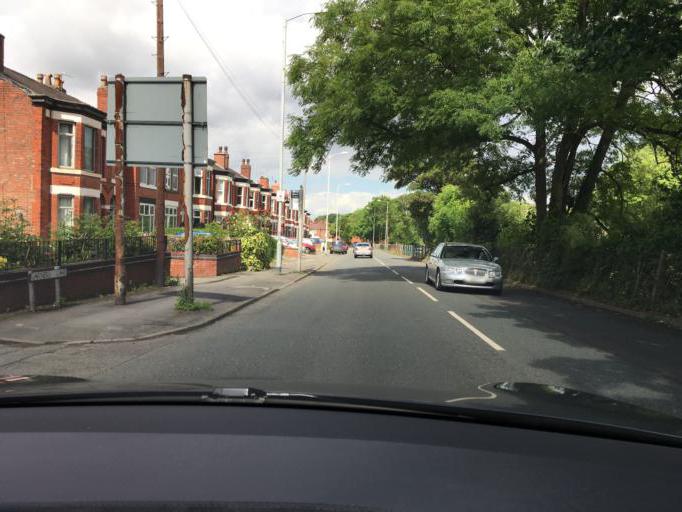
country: GB
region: England
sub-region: Borough of Stockport
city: Stockport
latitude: 53.3914
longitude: -2.1542
